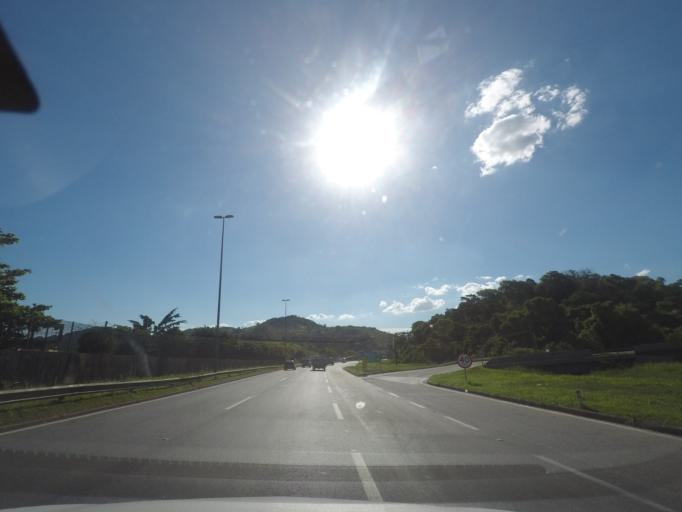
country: BR
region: Rio de Janeiro
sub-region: Petropolis
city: Petropolis
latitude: -22.6568
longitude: -43.1280
